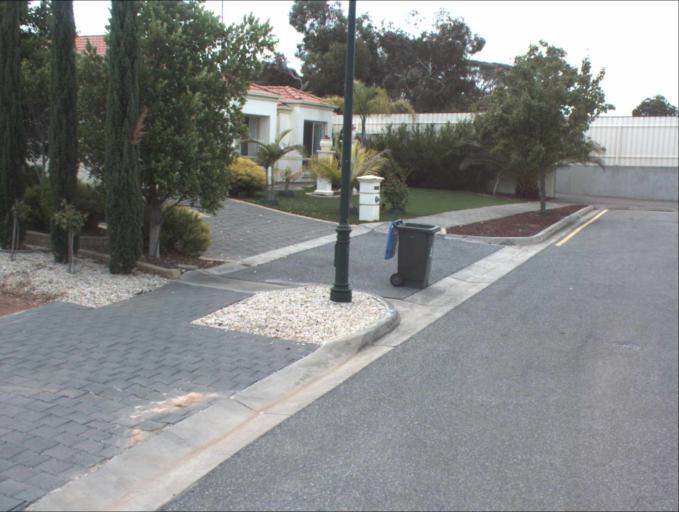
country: AU
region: South Australia
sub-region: Port Adelaide Enfield
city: Gilles Plains
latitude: -34.8442
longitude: 138.6480
